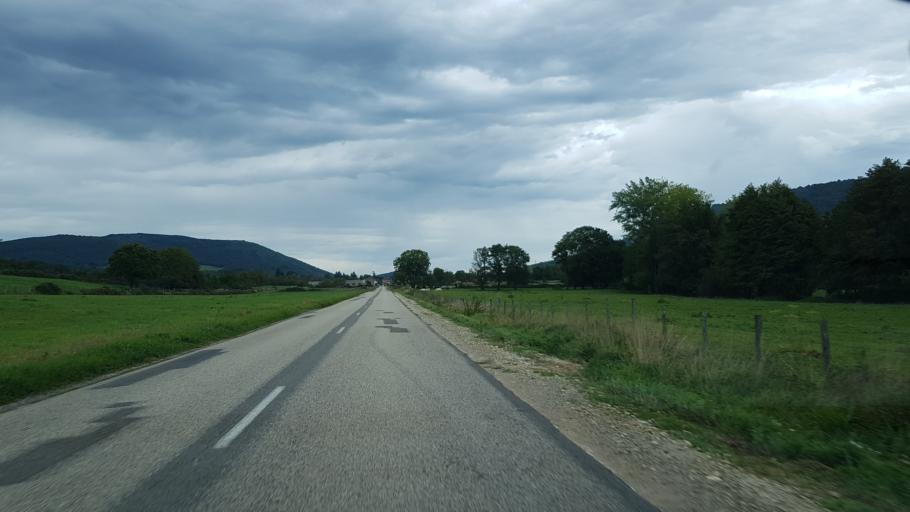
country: FR
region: Rhone-Alpes
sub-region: Departement de l'Ain
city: Cuisiat
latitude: 46.2535
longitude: 5.4242
